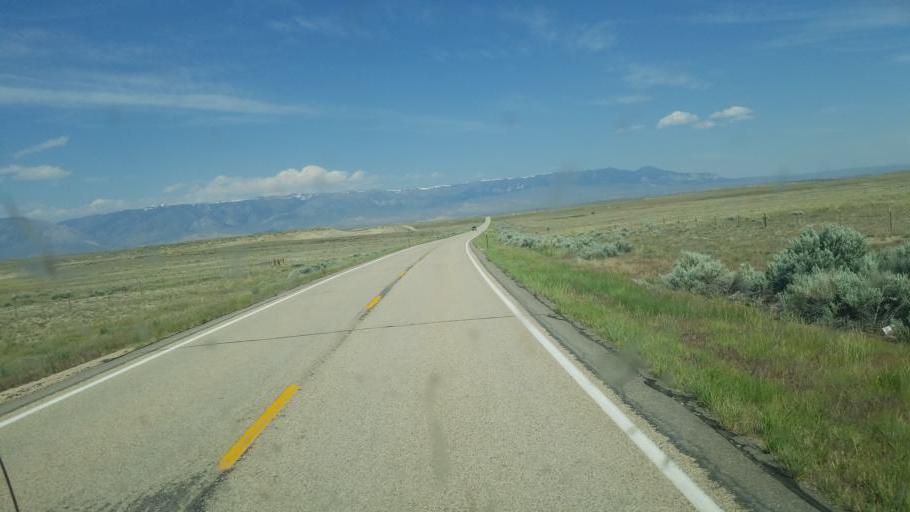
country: US
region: Wyoming
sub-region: Park County
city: Powell
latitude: 44.8487
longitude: -109.0066
